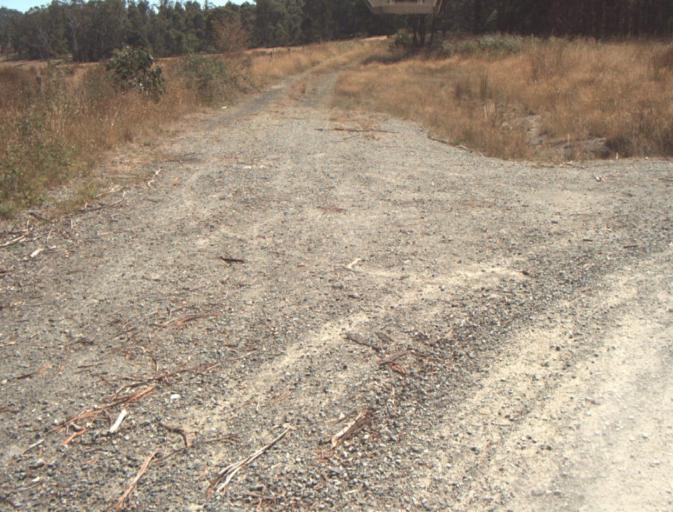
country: AU
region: Tasmania
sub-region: Launceston
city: Mayfield
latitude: -41.2488
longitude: 147.1835
